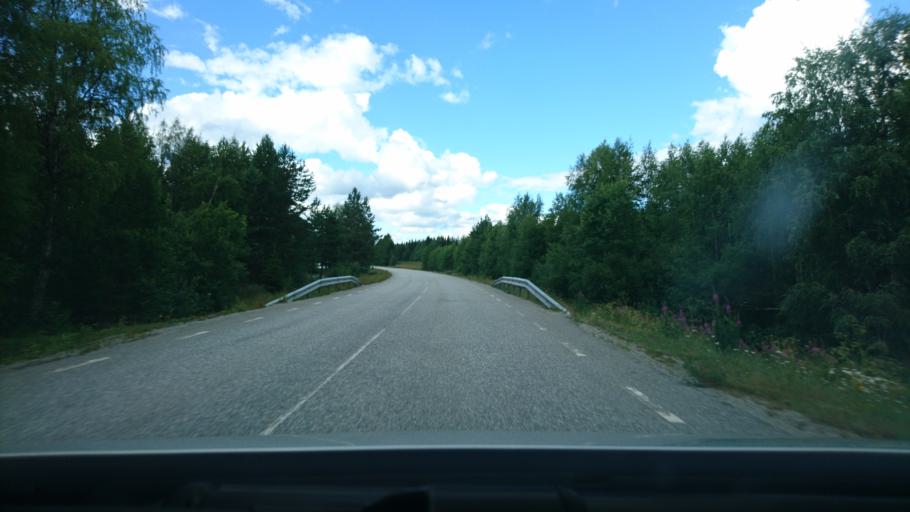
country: SE
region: Vaesterbotten
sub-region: Asele Kommun
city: Asele
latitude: 63.9751
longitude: 17.2637
